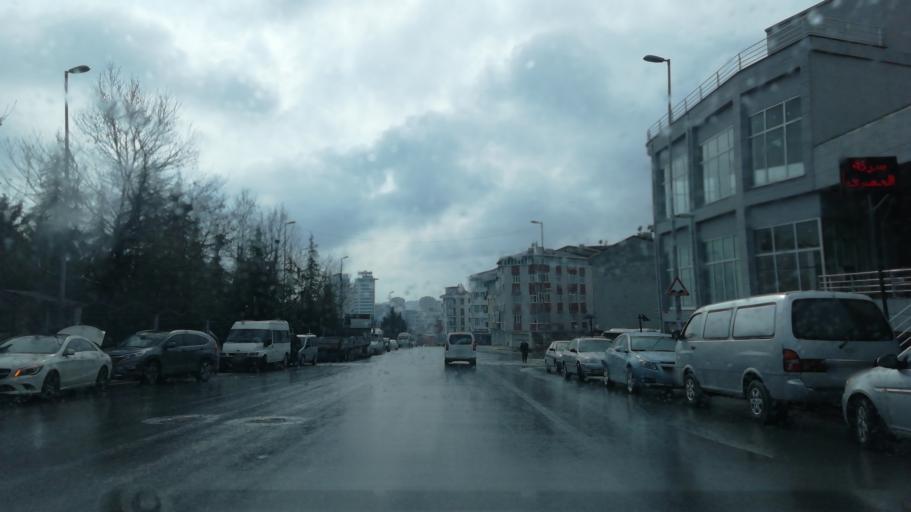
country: TR
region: Istanbul
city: Esenyurt
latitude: 41.0262
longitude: 28.6826
